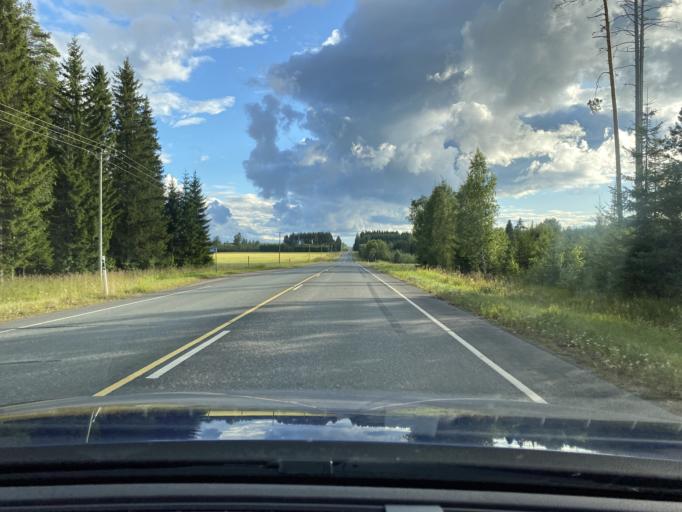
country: FI
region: Haeme
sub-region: Haemeenlinna
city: Renko
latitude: 60.8874
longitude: 24.2524
